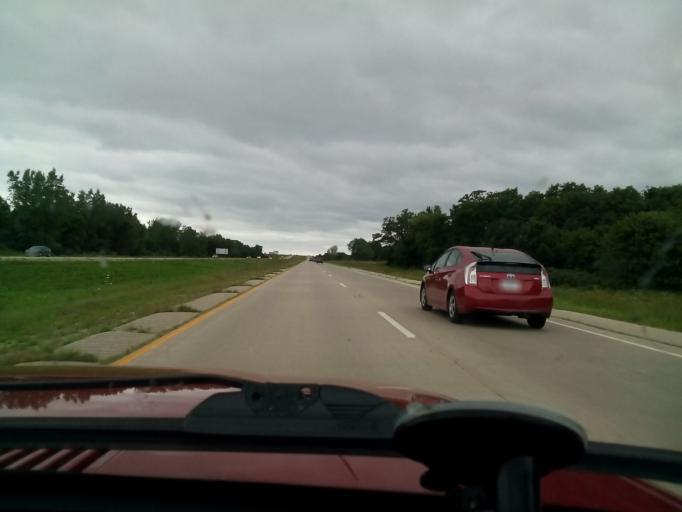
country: US
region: Wisconsin
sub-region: Columbia County
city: Columbus
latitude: 43.3007
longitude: -89.0570
